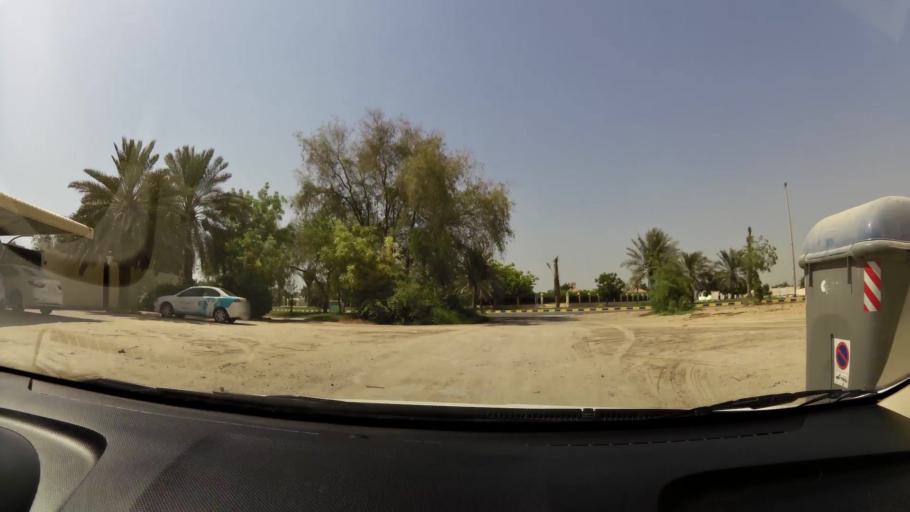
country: AE
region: Ajman
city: Ajman
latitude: 25.4214
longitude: 55.4714
